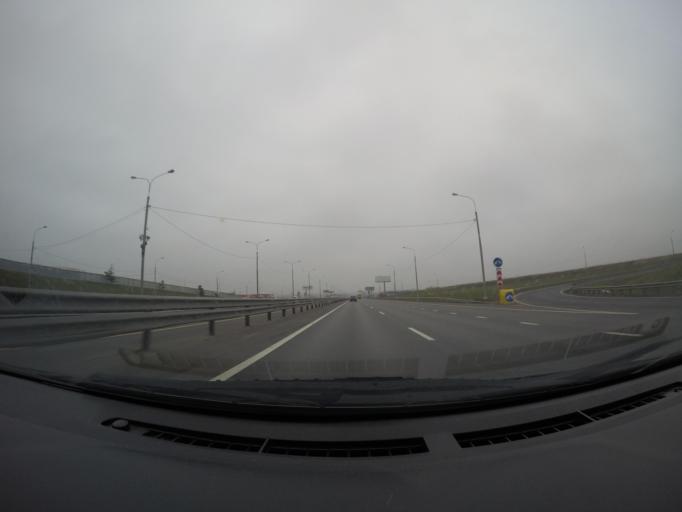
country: RU
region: Moskovskaya
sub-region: Podol'skiy Rayon
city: Podol'sk
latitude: 55.4384
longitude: 37.6162
